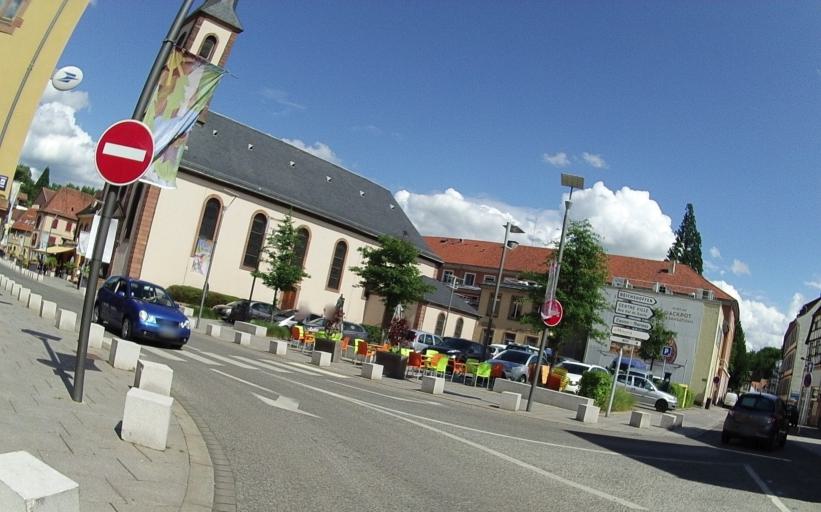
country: FR
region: Alsace
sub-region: Departement du Bas-Rhin
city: Niederbronn-les-Bains
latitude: 48.9505
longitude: 7.6416
